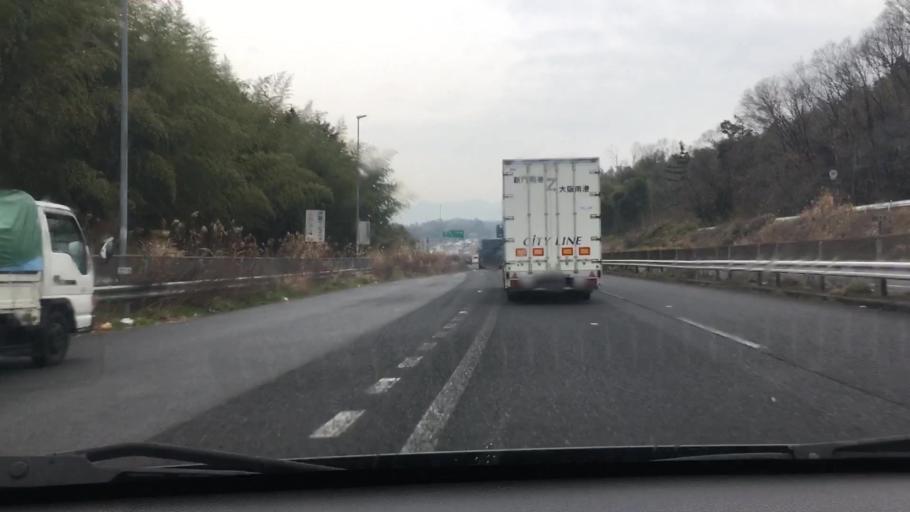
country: JP
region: Mie
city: Ueno-ebisumachi
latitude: 34.8148
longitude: 136.2121
